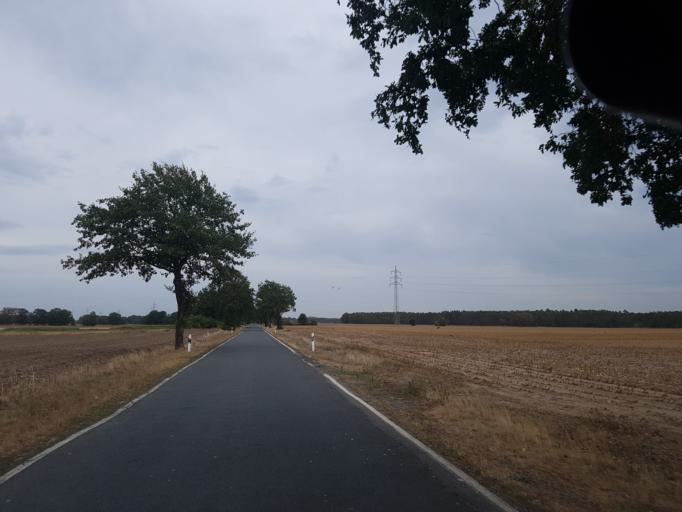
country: DE
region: Saxony-Anhalt
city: Annaburg
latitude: 51.7759
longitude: 13.0577
